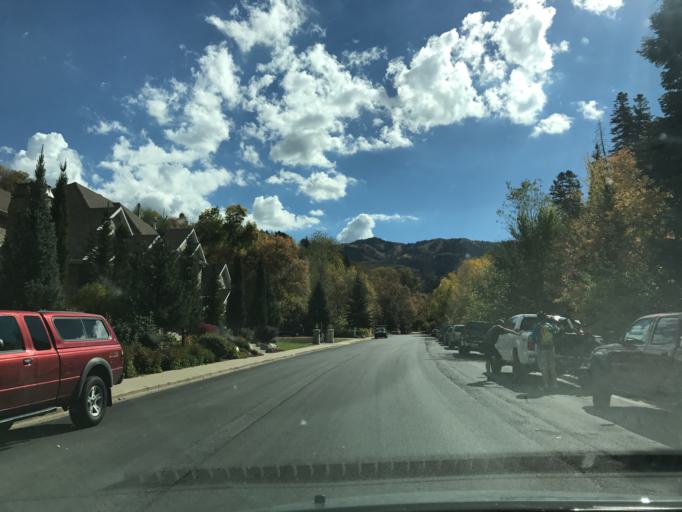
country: US
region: Utah
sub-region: Davis County
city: Bountiful
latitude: 40.8652
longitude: -111.8394
